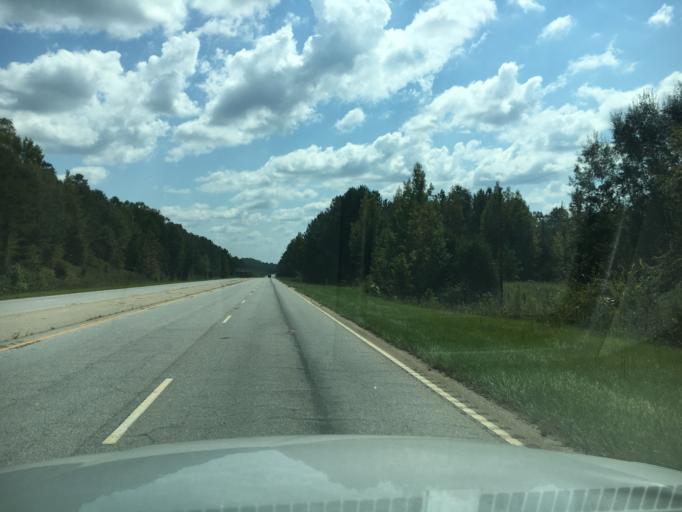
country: US
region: South Carolina
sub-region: Greenwood County
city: Ware Shoals
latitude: 34.4165
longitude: -82.2313
